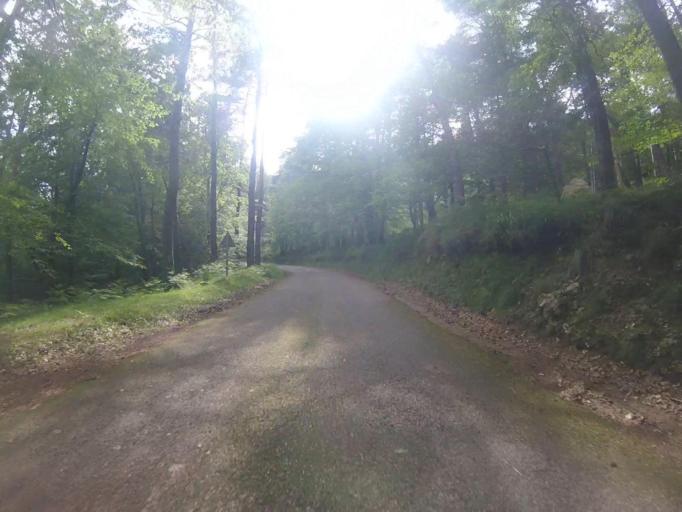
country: ES
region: Navarre
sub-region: Provincia de Navarra
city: Goizueta
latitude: 43.2316
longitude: -1.8058
